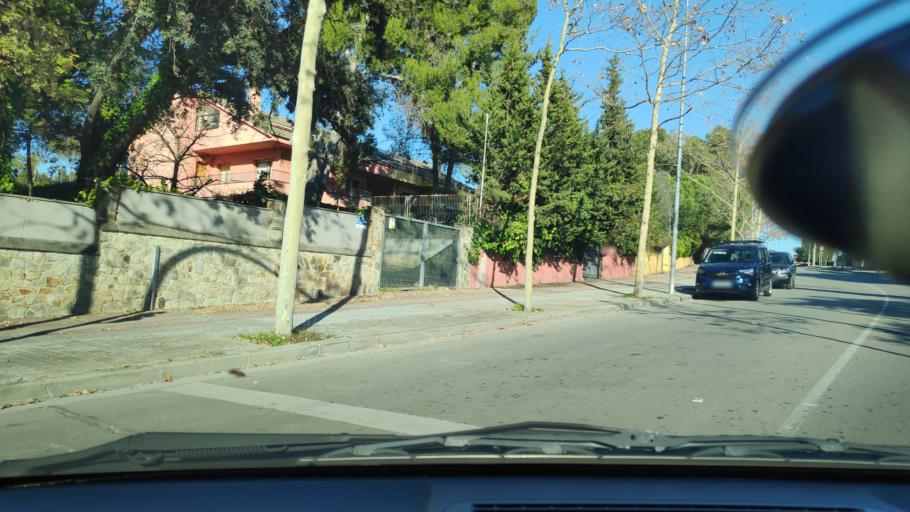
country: ES
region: Catalonia
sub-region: Provincia de Barcelona
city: Sant Quirze del Valles
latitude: 41.5572
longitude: 2.0728
